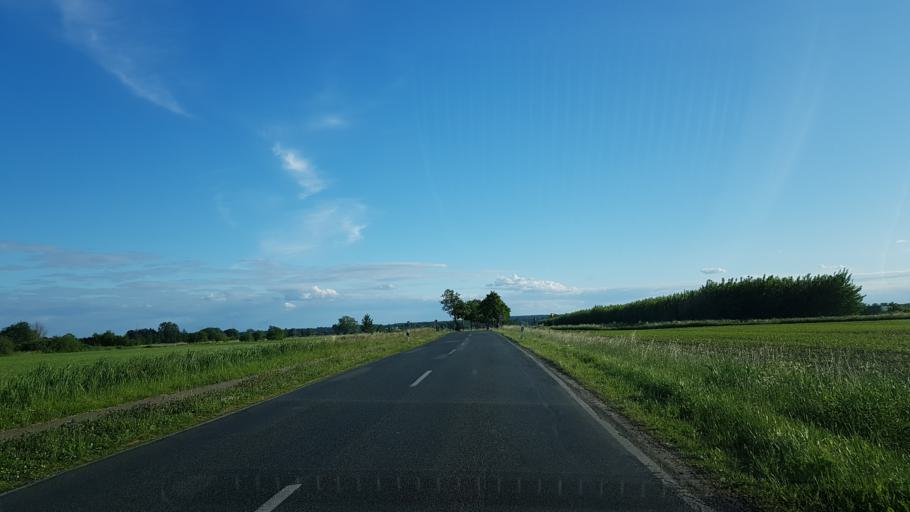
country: DE
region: Lower Saxony
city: Stelle
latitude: 53.4077
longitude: 10.1361
